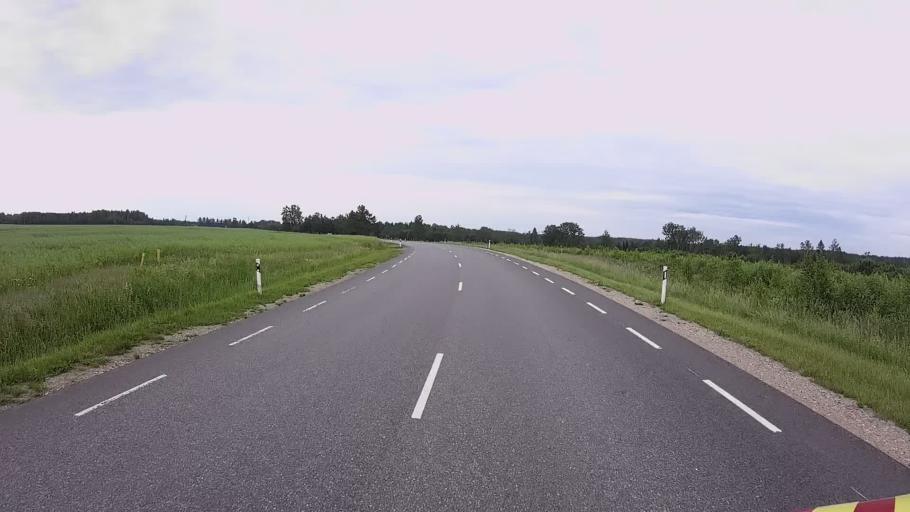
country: EE
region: Viljandimaa
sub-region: Karksi vald
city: Karksi-Nuia
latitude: 58.1702
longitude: 25.5800
